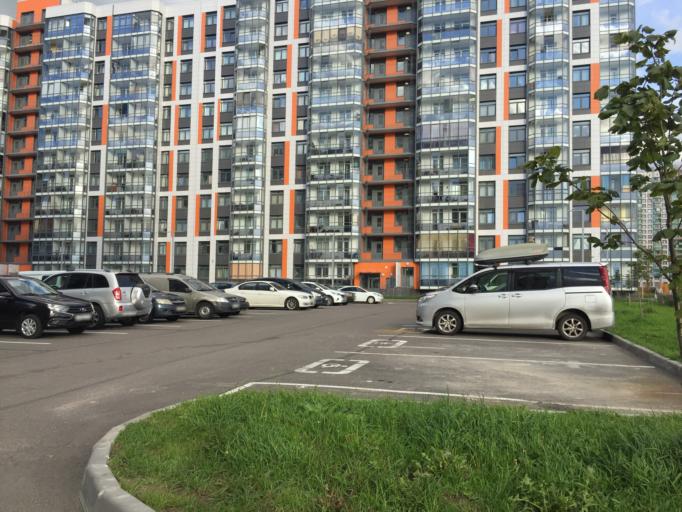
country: RU
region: St.-Petersburg
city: Grazhdanka
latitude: 60.0579
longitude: 30.4155
